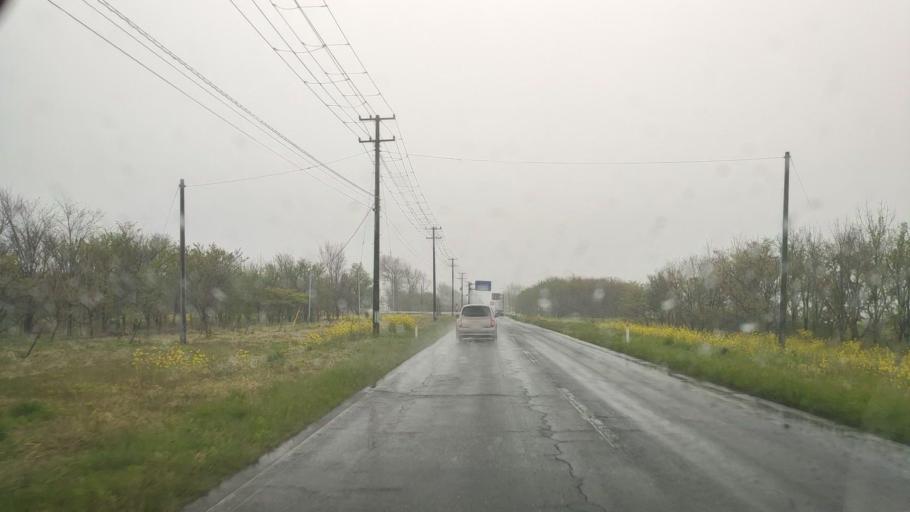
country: JP
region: Akita
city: Tenno
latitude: 39.9932
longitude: 139.9463
